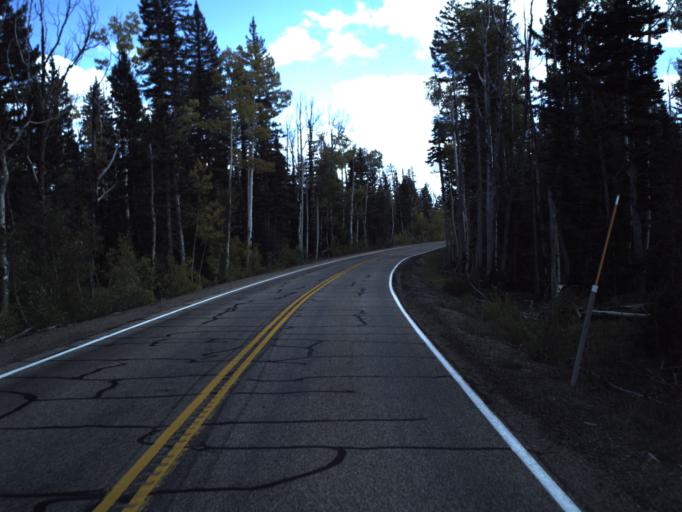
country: US
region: Utah
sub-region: Iron County
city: Parowan
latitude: 37.5210
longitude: -112.7292
